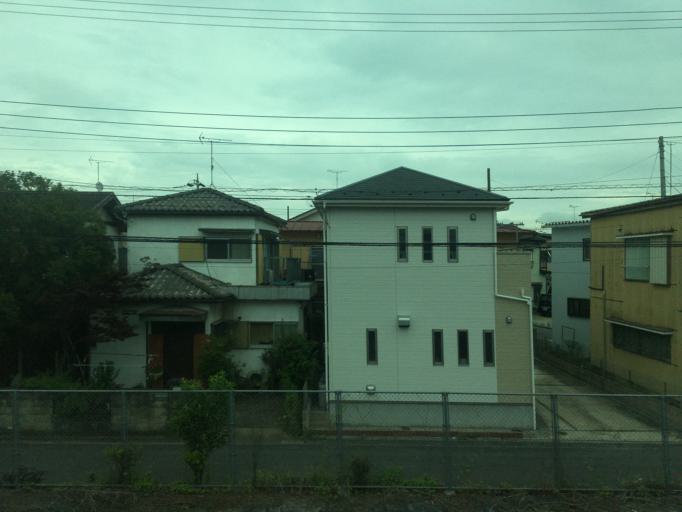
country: JP
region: Saitama
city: Hasuda
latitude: 35.9523
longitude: 139.6411
